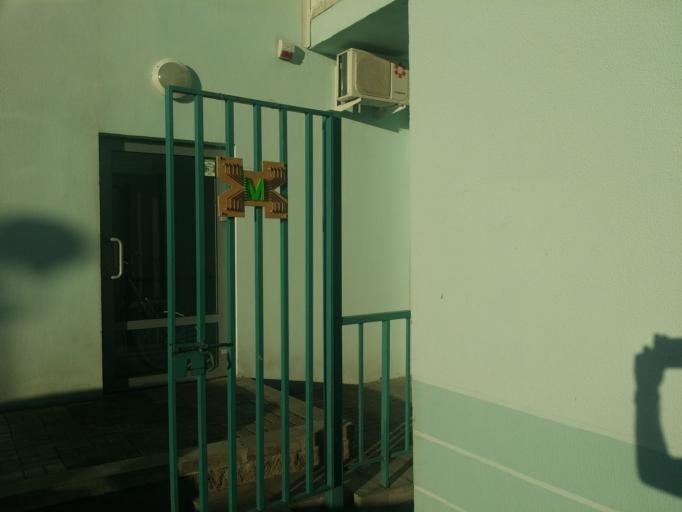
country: BY
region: Minsk
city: Minsk
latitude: 53.9430
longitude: 27.5977
